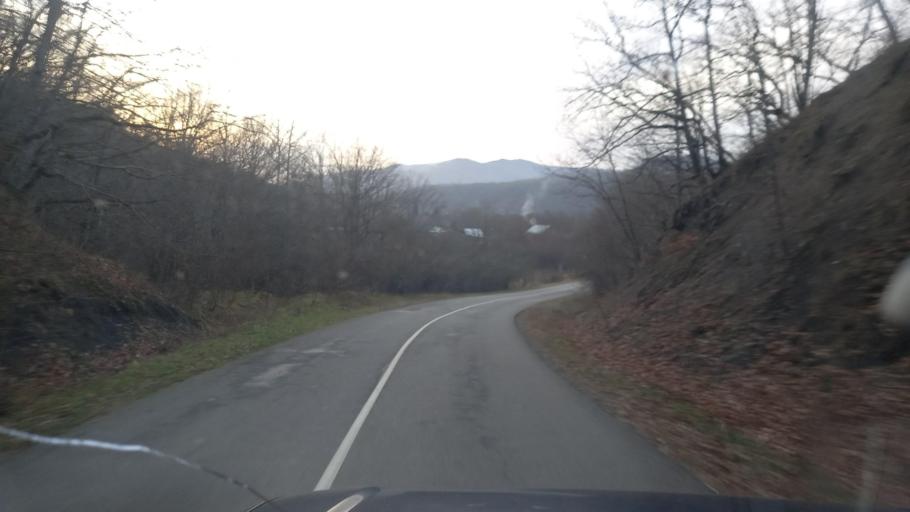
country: RU
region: Krasnodarskiy
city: Goryachiy Klyuch
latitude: 44.3878
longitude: 39.1785
